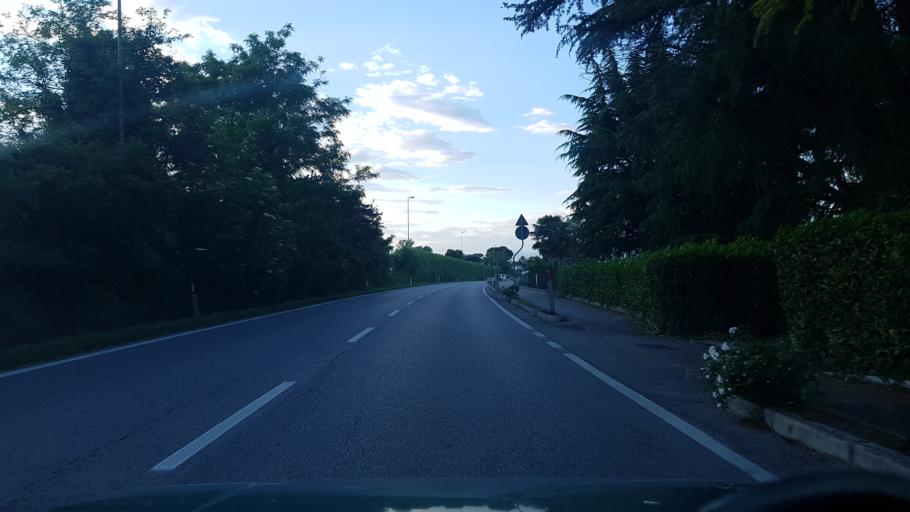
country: IT
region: Friuli Venezia Giulia
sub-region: Provincia di Udine
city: Santa Maria la Longa
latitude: 45.9172
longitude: 13.2945
